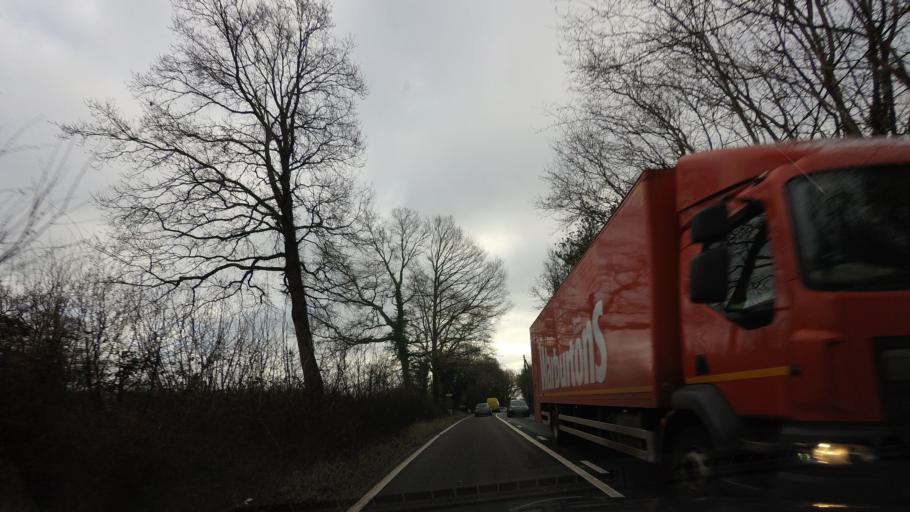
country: GB
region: England
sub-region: East Sussex
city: Wadhurst
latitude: 51.0819
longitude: 0.4164
